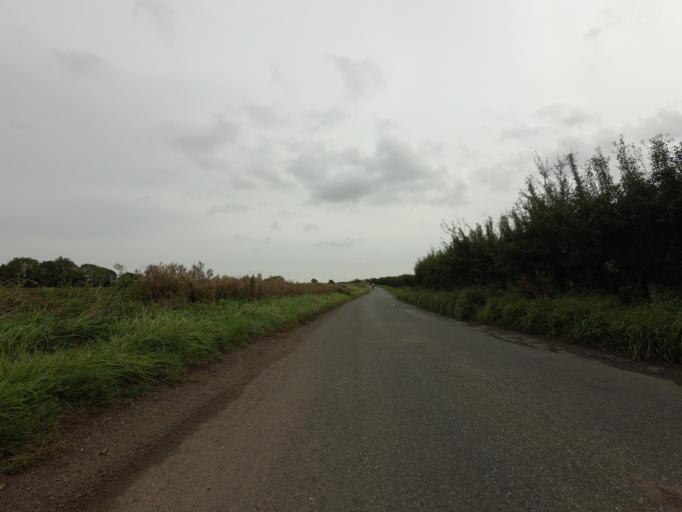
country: GB
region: England
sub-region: Hertfordshire
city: Buntingford
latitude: 51.9767
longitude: 0.0623
